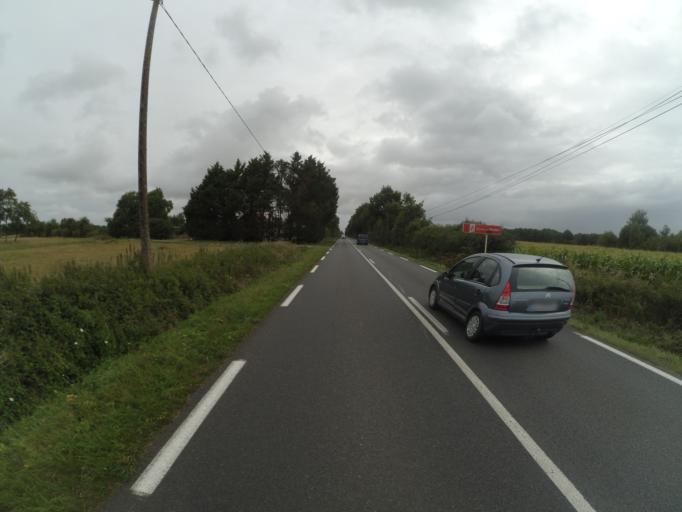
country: FR
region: Pays de la Loire
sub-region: Departement de la Vendee
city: Rocheserviere
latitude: 46.9213
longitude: -1.5358
